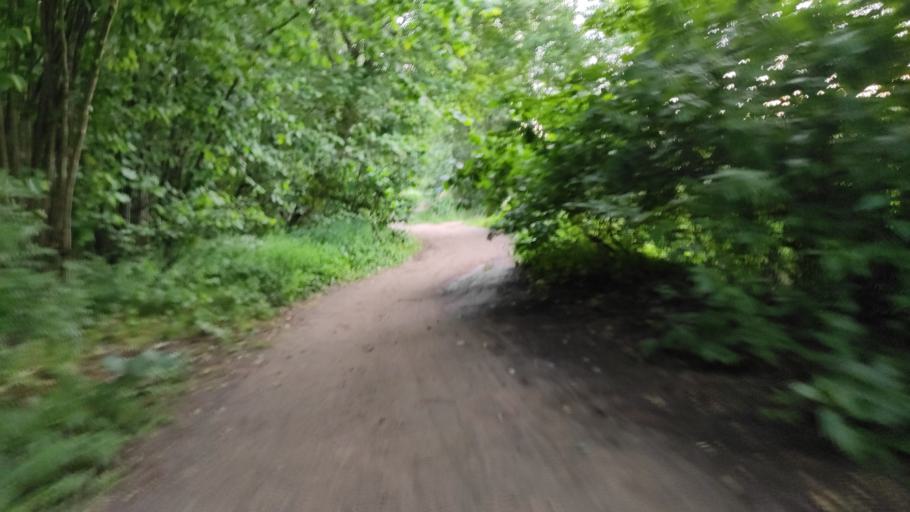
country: BY
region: Minsk
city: Zhdanovichy
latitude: 53.9630
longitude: 27.4352
